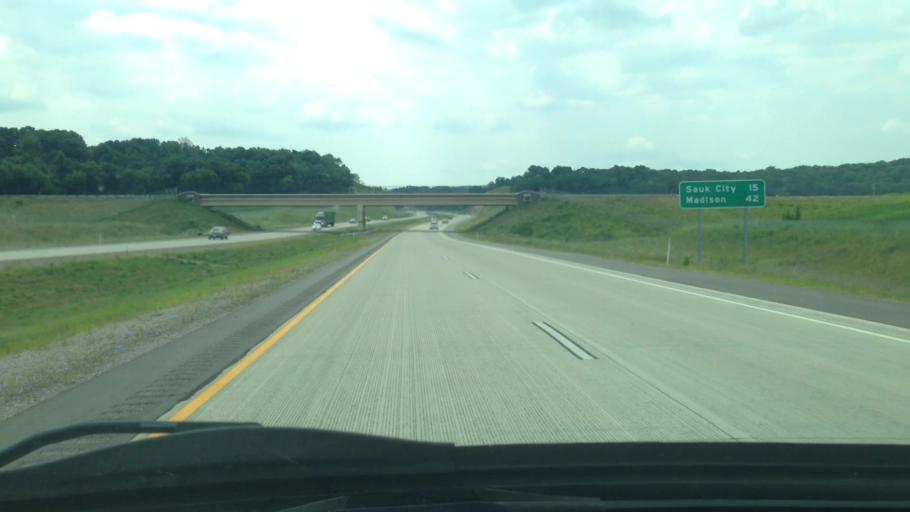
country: US
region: Wisconsin
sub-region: Sauk County
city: West Baraboo
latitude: 43.4474
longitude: -89.7781
